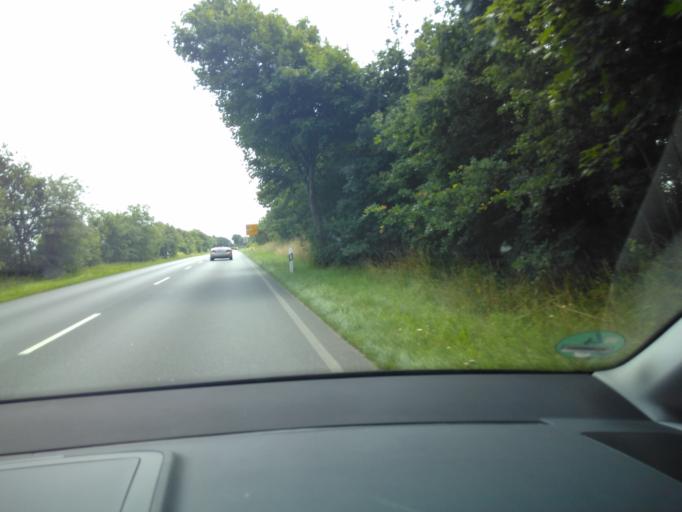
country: DE
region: Lower Saxony
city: Midlum
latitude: 53.7655
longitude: 8.6311
